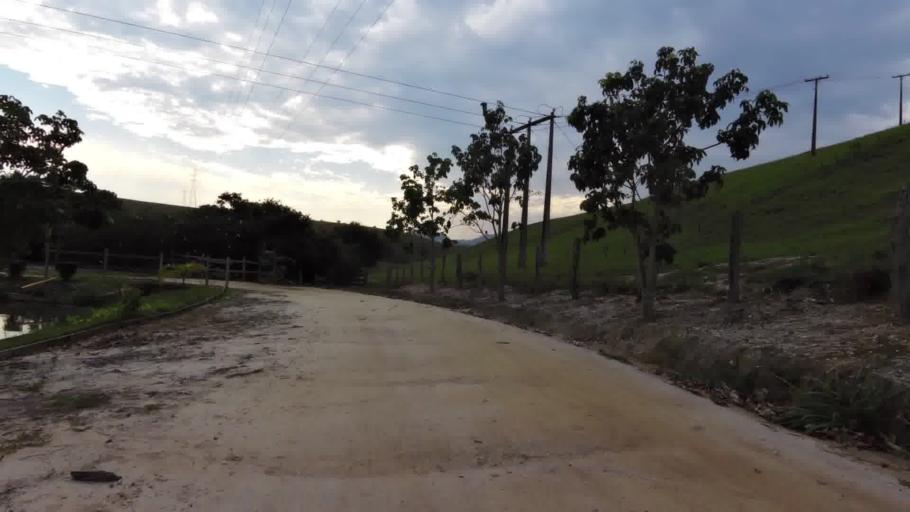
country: BR
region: Espirito Santo
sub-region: Piuma
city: Piuma
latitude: -20.8283
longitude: -40.7457
